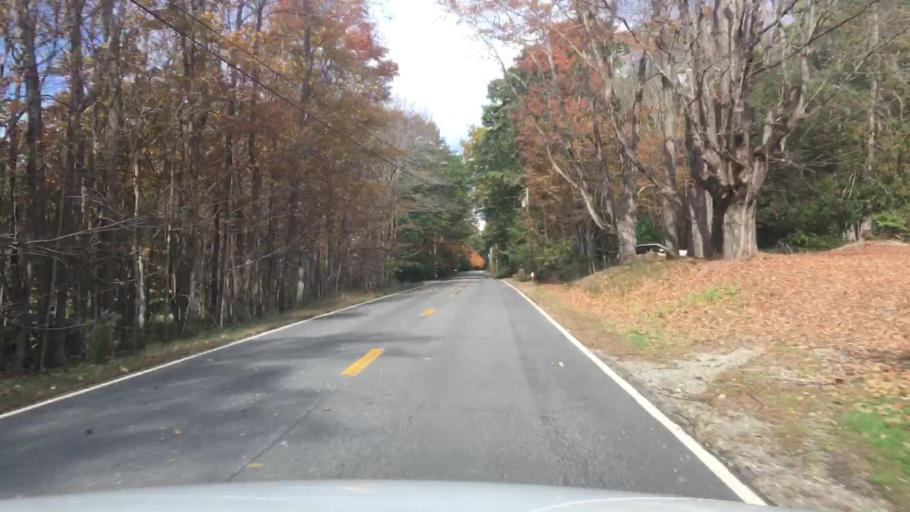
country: US
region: Maine
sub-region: Knox County
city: Hope
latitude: 44.3162
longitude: -69.1223
